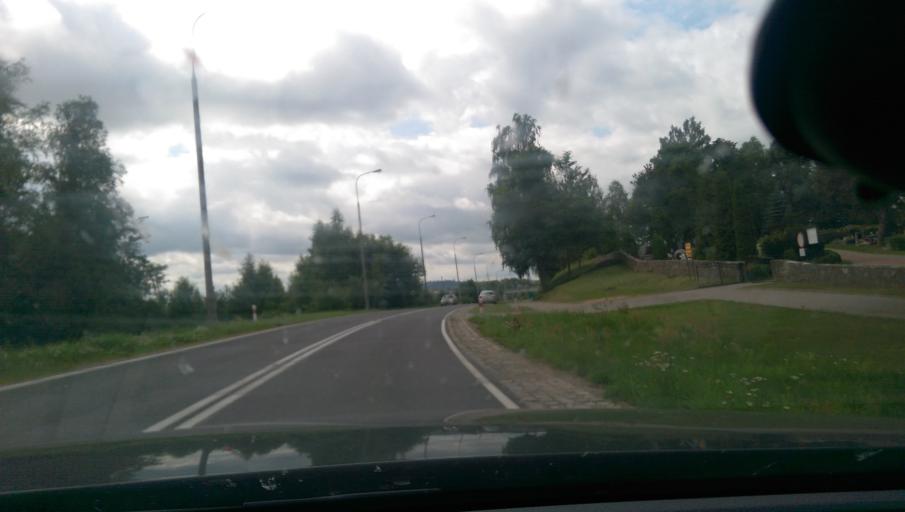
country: PL
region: Warmian-Masurian Voivodeship
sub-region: Powiat goldapski
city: Goldap
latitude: 54.3241
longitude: 22.2983
